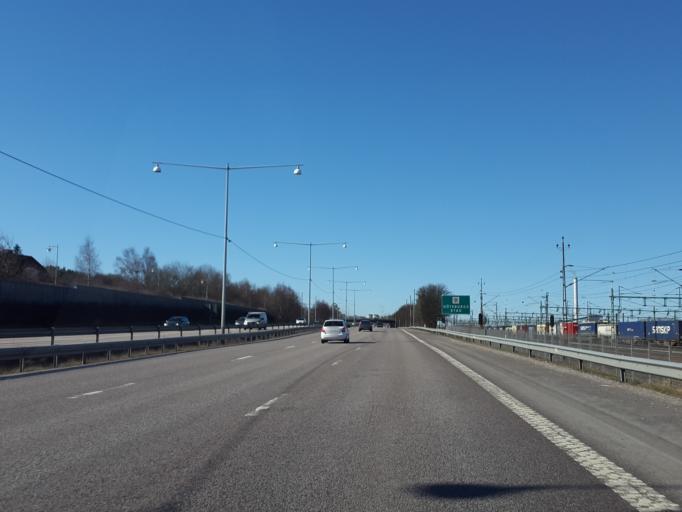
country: SE
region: Vaestra Goetaland
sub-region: Goteborg
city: Eriksbo
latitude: 57.7313
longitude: 12.0576
